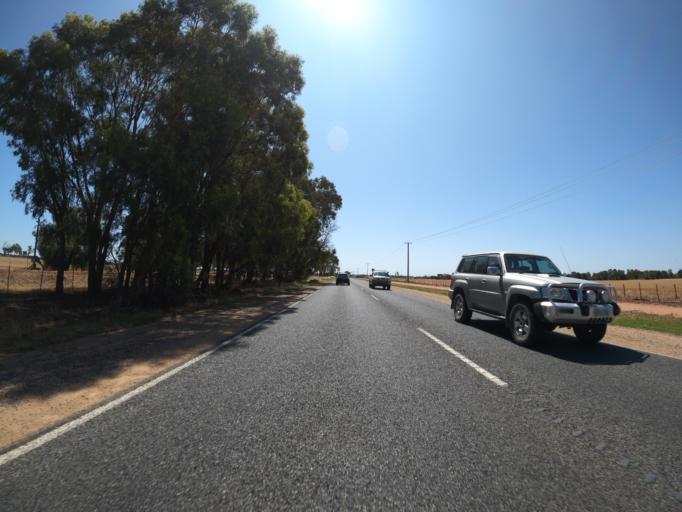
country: AU
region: Victoria
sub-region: Moira
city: Yarrawonga
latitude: -36.0195
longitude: 146.0535
